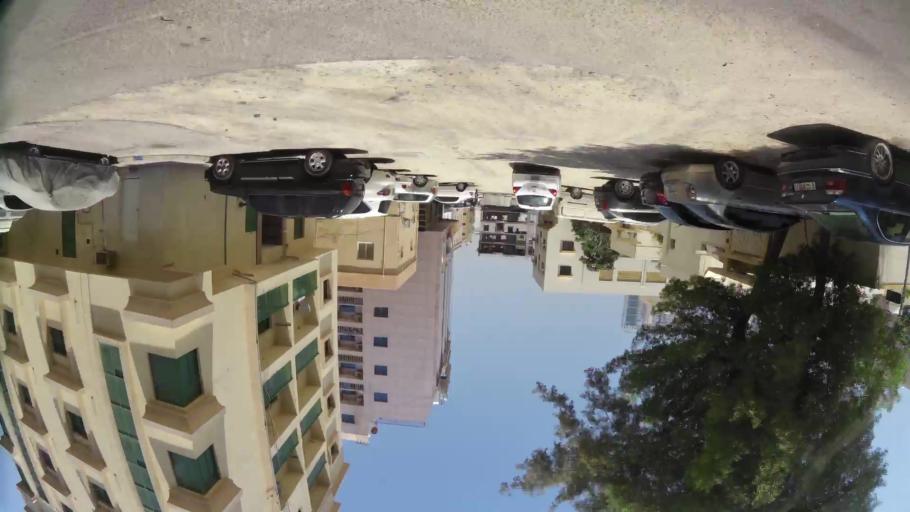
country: AE
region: Ajman
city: Ajman
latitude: 25.4052
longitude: 55.4329
